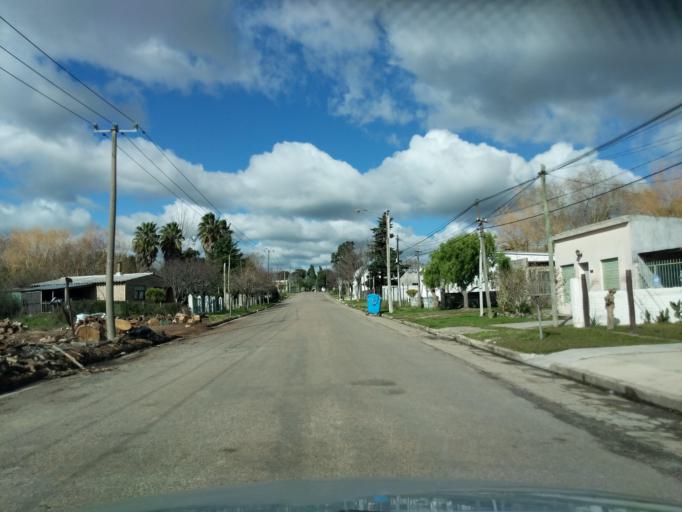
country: UY
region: Florida
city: Florida
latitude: -34.0930
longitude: -56.2340
